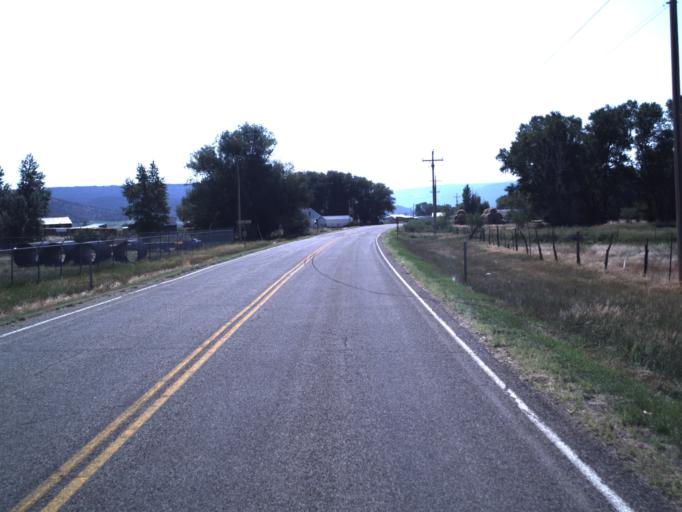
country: US
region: Utah
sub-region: Duchesne County
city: Duchesne
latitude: 40.3502
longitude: -110.7066
